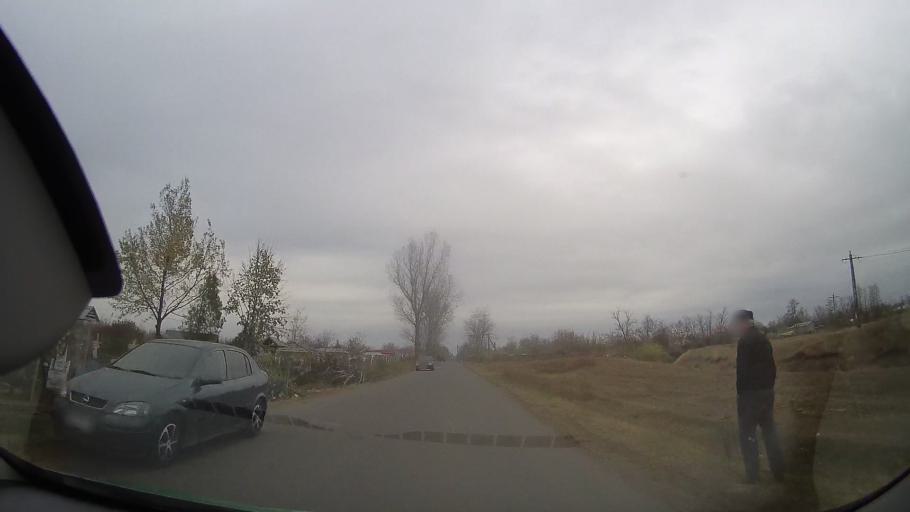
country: RO
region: Braila
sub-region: Comuna Rosiori
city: Rosiori
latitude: 44.8098
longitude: 27.3749
